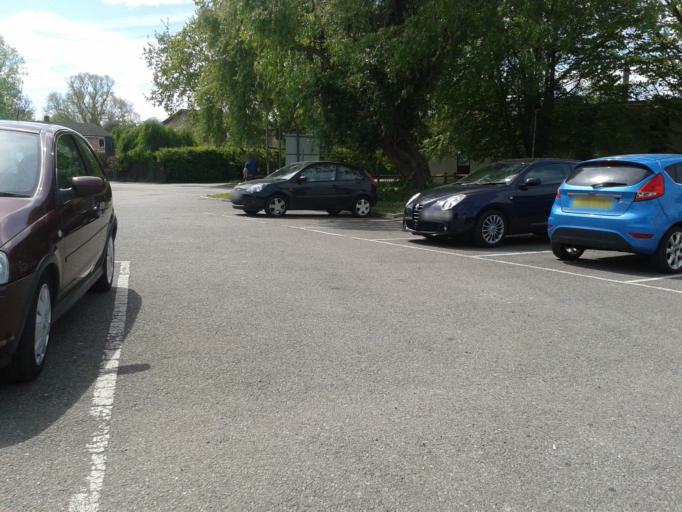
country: GB
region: England
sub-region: Cambridgeshire
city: Meldreth
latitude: 52.1141
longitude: 0.0314
